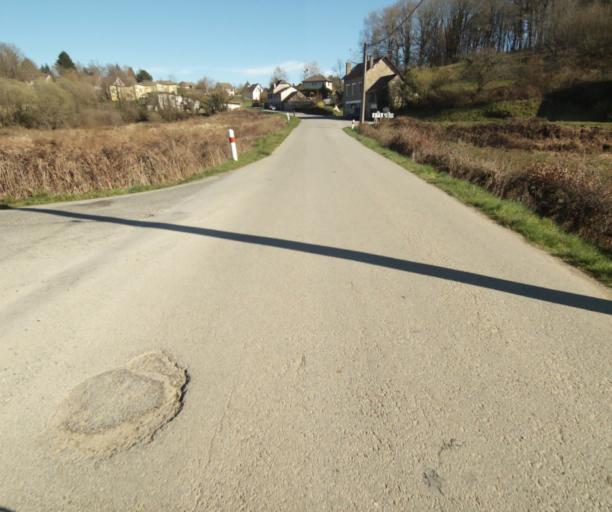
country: FR
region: Limousin
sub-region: Departement de la Correze
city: Chamboulive
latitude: 45.4698
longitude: 1.7230
